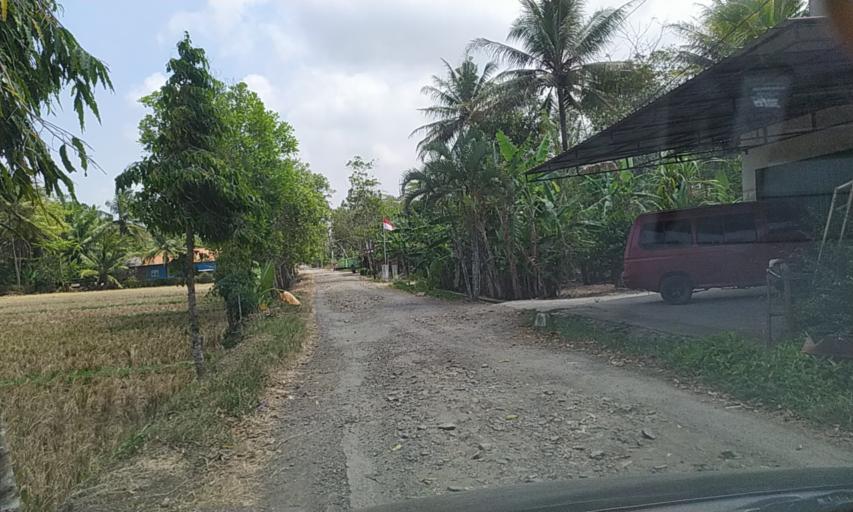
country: ID
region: Central Java
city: Sawoan
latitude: -7.6340
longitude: 109.0621
